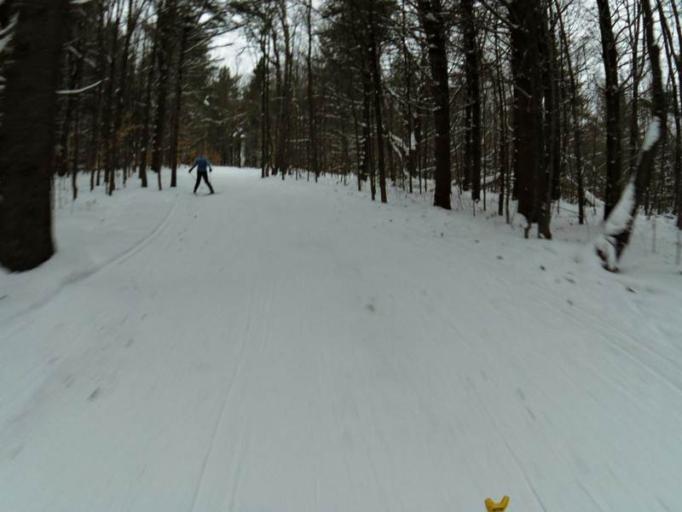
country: CA
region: Quebec
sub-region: Outaouais
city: Gatineau
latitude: 45.4942
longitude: -75.8434
